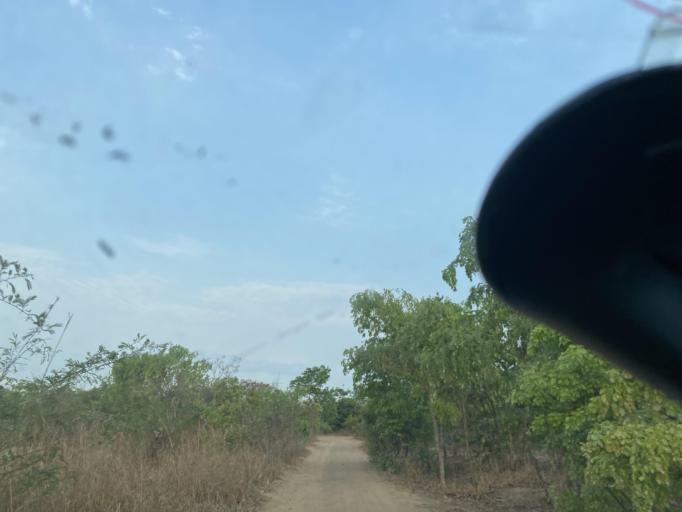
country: ZM
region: Lusaka
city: Chongwe
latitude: -15.2080
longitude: 28.5097
